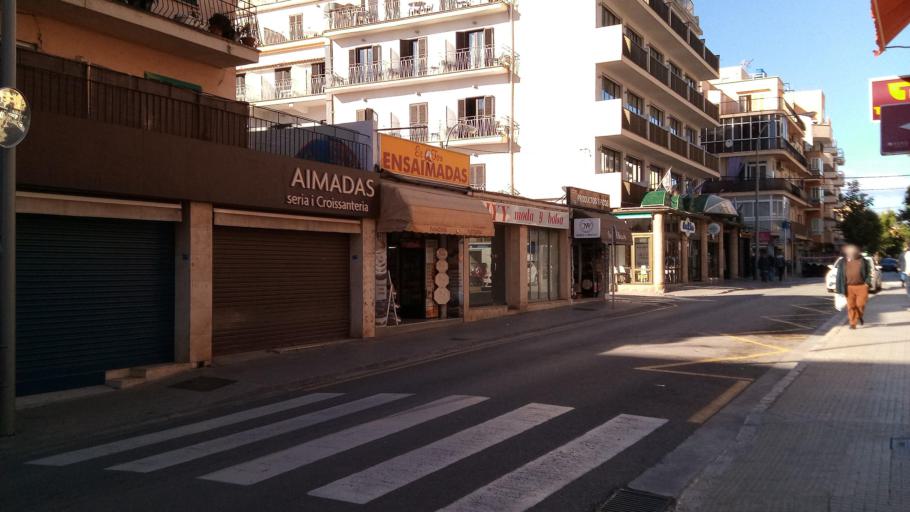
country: ES
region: Balearic Islands
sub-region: Illes Balears
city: s'Arenal
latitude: 39.5366
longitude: 2.7183
